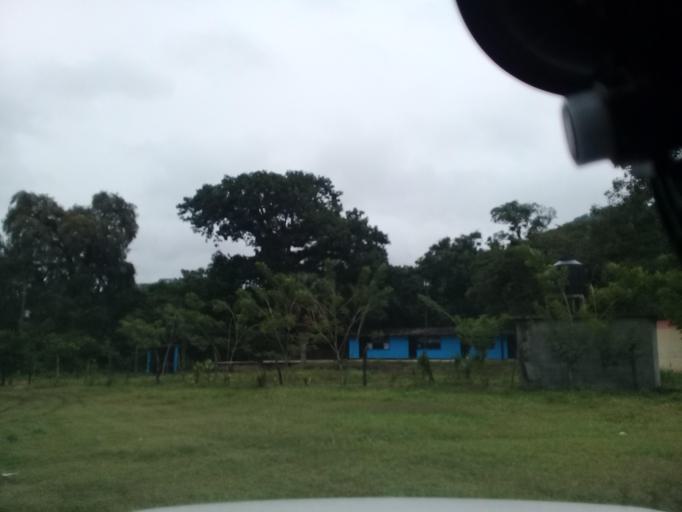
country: MX
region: Veracruz
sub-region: Chalma
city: San Pedro Coyutla
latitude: 21.2060
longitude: -98.3964
